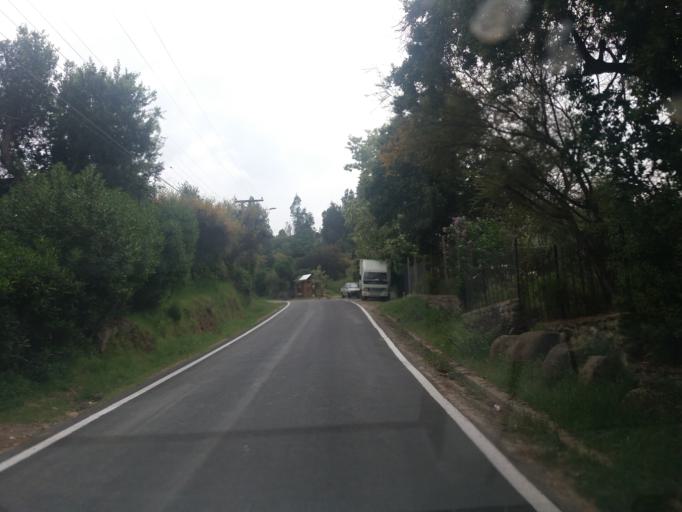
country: CL
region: Valparaiso
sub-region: Provincia de Marga Marga
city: Limache
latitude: -33.0291
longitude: -71.0788
